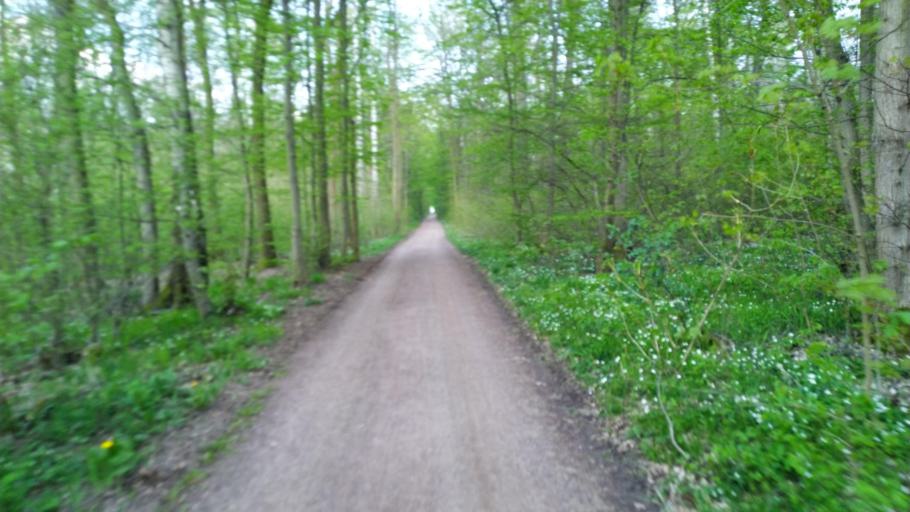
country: DE
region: Thuringia
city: Kromsdorf
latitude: 50.9826
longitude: 11.3606
